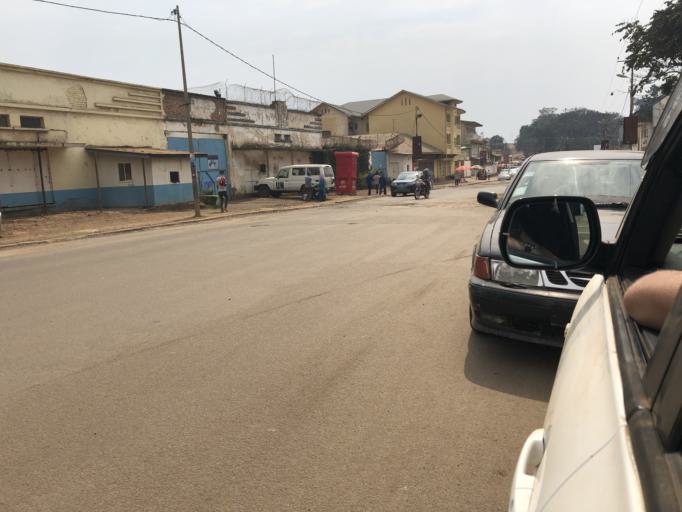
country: CD
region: South Kivu
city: Bukavu
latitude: -2.5023
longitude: 28.8705
